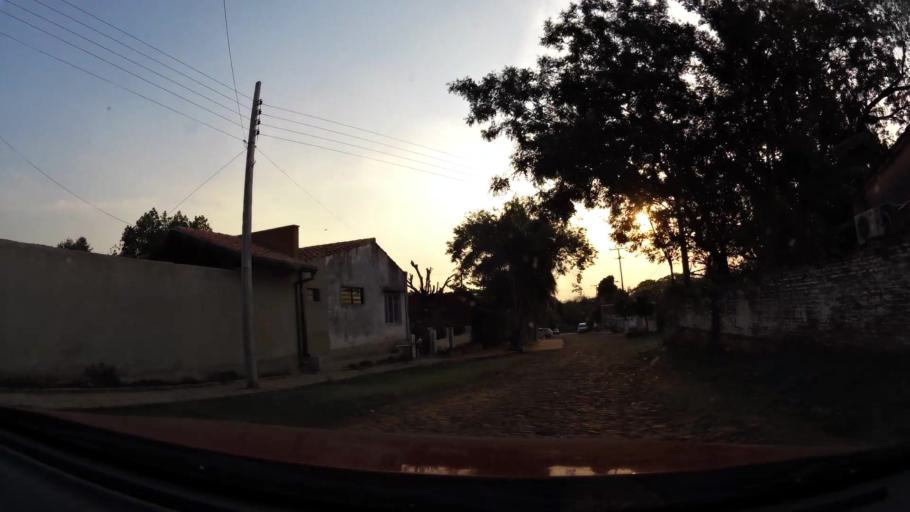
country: PY
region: Central
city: Lambare
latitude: -25.3460
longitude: -57.6003
